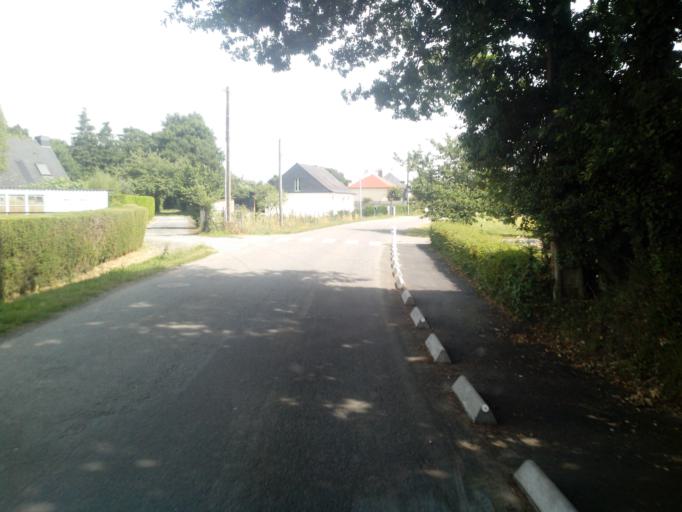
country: FR
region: Brittany
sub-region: Departement d'Ille-et-Vilaine
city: Messac
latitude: 47.8191
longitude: -1.8171
